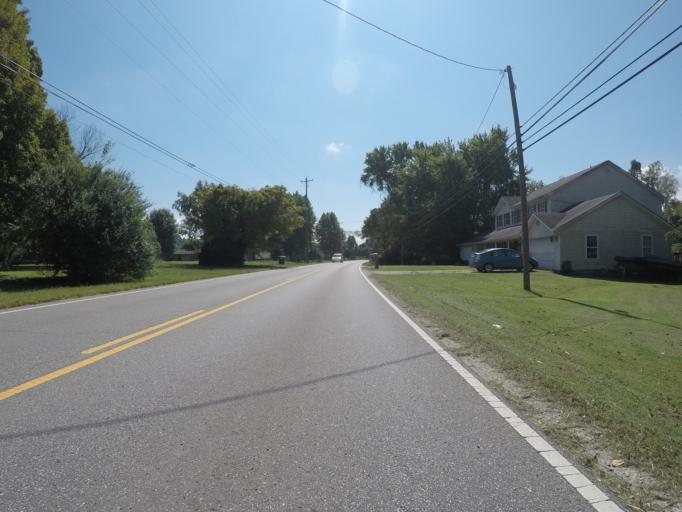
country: US
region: Kentucky
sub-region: Boyd County
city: Ashland
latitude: 38.4601
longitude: -82.5981
